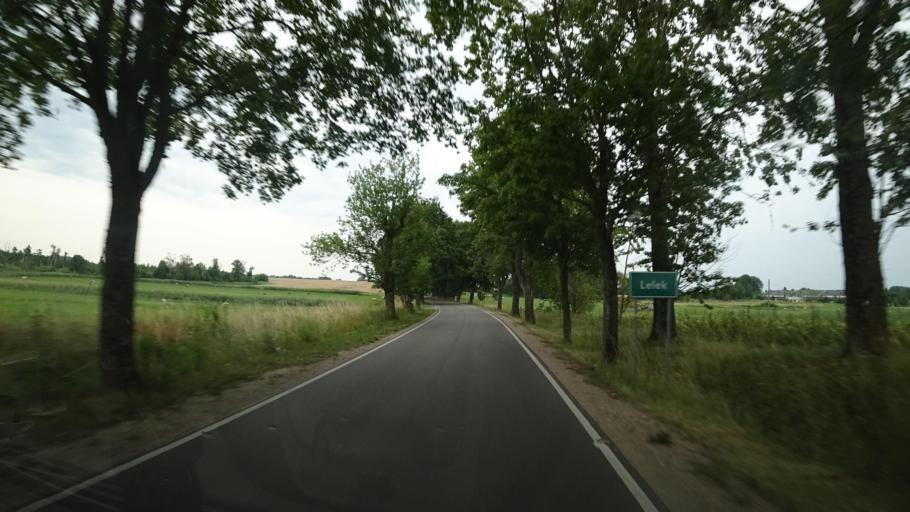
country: PL
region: Warmian-Masurian Voivodeship
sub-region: Powiat mragowski
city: Mikolajki
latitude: 53.8661
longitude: 21.5980
